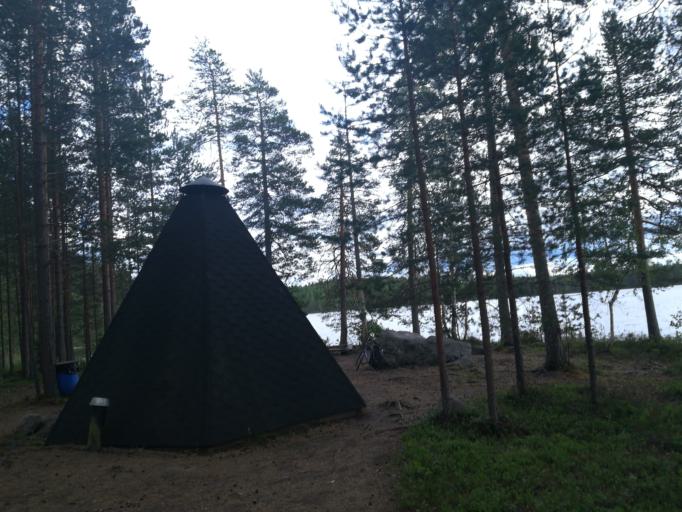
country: FI
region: Southern Savonia
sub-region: Mikkeli
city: Mikkeli
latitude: 61.6712
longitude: 27.1114
